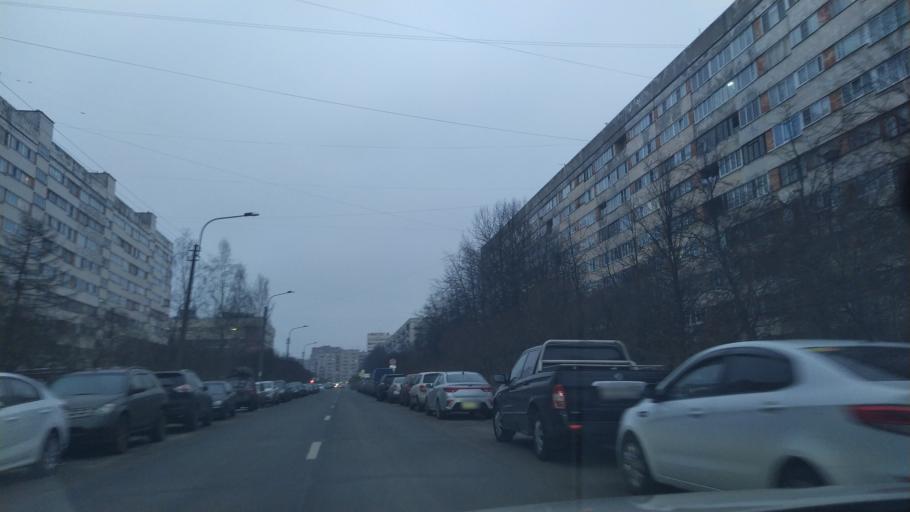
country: RU
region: St.-Petersburg
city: Grazhdanka
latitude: 60.0450
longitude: 30.3990
